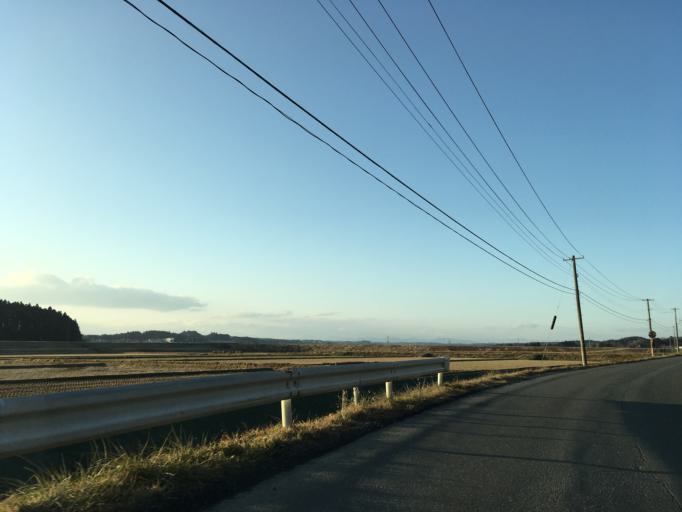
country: JP
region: Iwate
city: Ichinoseki
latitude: 38.8090
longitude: 141.2154
